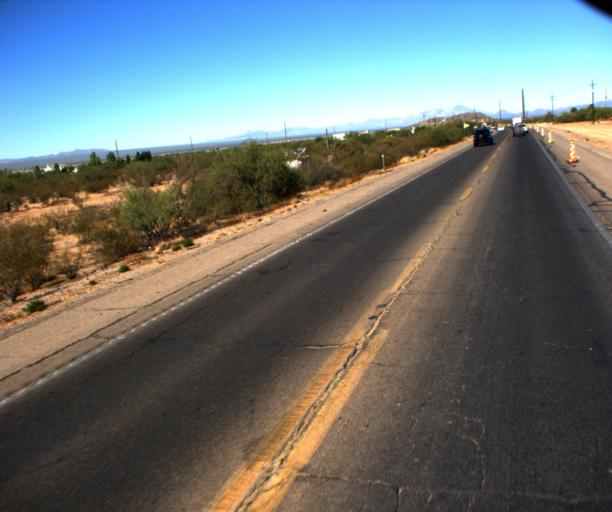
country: US
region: Arizona
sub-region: Pima County
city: Tucson Estates
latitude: 32.1653
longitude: -111.0932
